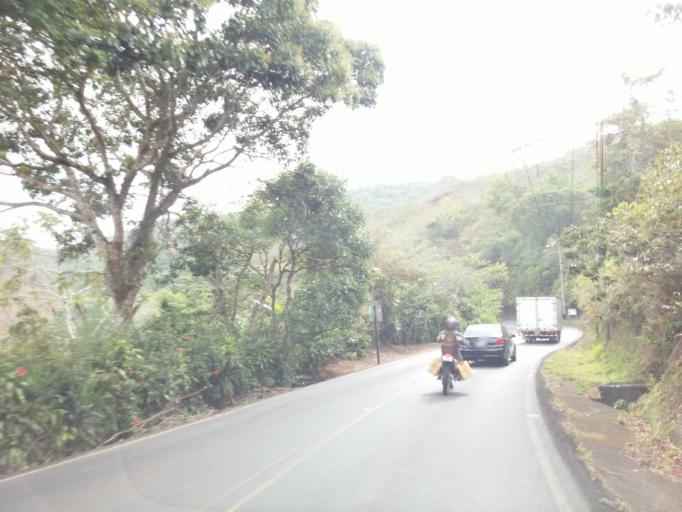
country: CR
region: Alajuela
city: San Ramon
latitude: 10.1213
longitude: -84.4708
